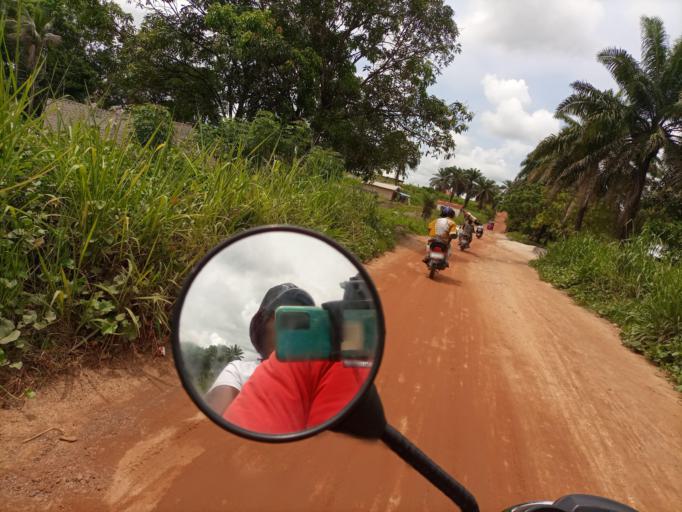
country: SL
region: Southern Province
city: Bo
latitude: 7.9714
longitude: -11.7180
